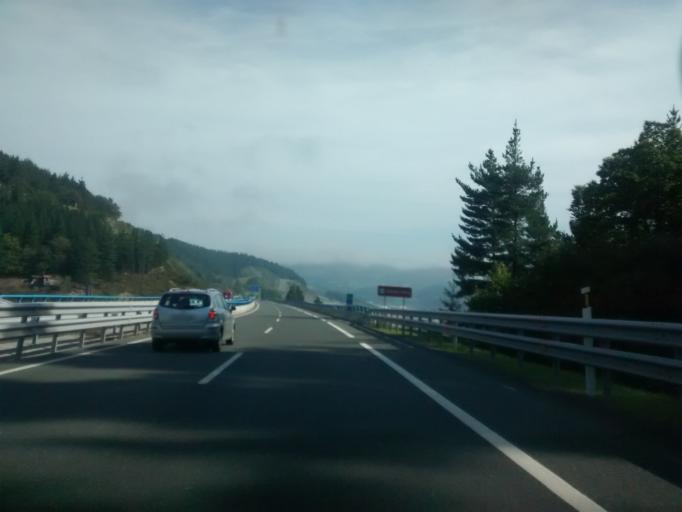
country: ES
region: Basque Country
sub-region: Provincia de Guipuzcoa
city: Eskoriatza
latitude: 43.0183
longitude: -2.5304
